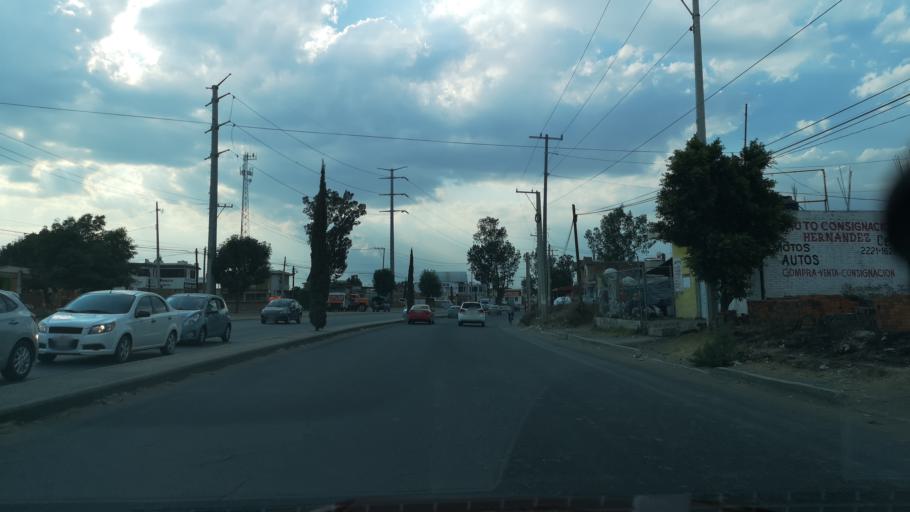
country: MX
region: Puebla
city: Cholula
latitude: 19.0789
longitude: -98.3258
